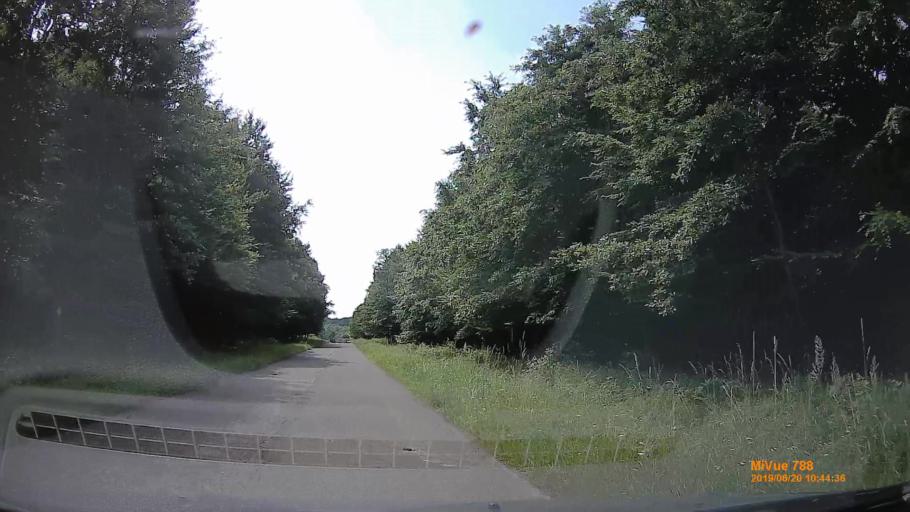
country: HU
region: Baranya
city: Hidas
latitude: 46.1874
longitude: 18.5668
